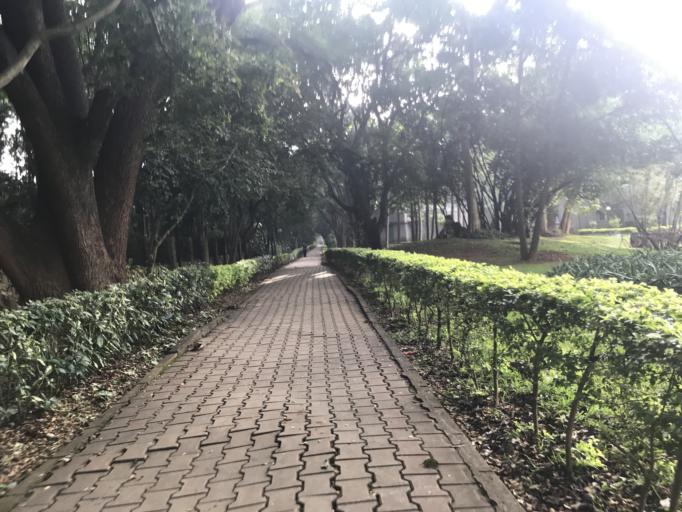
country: IN
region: Karnataka
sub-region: Bangalore Urban
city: Yelahanka
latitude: 13.0728
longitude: 77.5789
